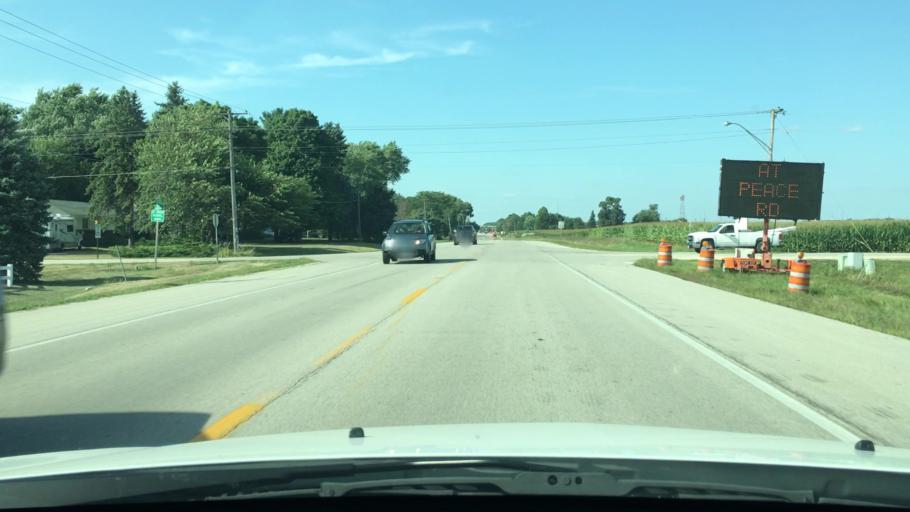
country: US
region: Illinois
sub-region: DeKalb County
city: DeKalb
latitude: 41.8924
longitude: -88.7536
